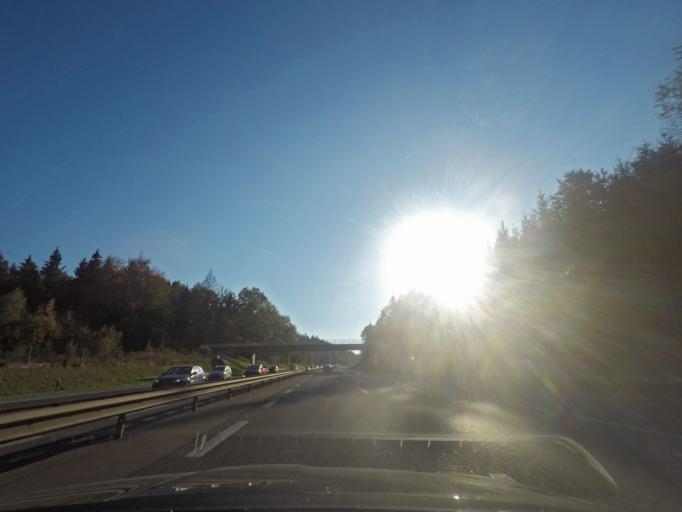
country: CH
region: Aargau
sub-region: Bezirk Aarau
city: Graenichen
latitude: 47.3795
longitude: 8.1088
